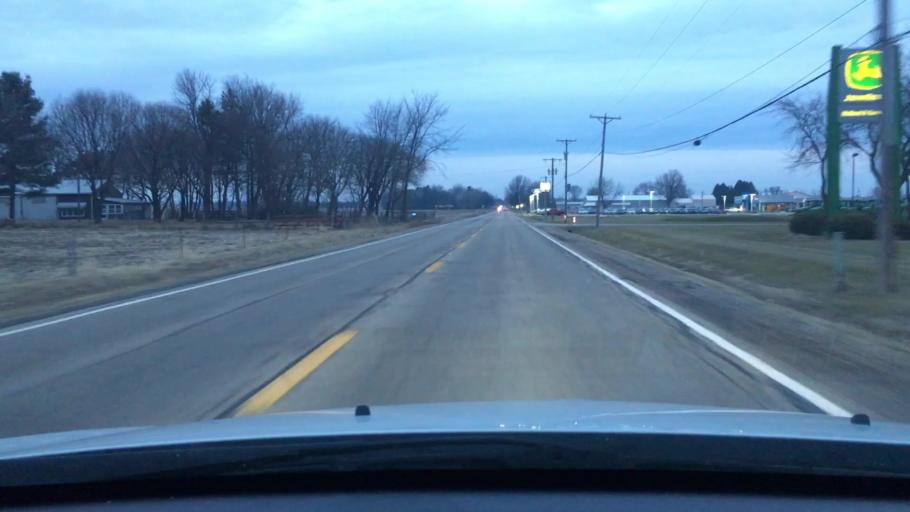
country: US
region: Illinois
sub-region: LaSalle County
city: Mendota
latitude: 41.5222
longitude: -89.1274
